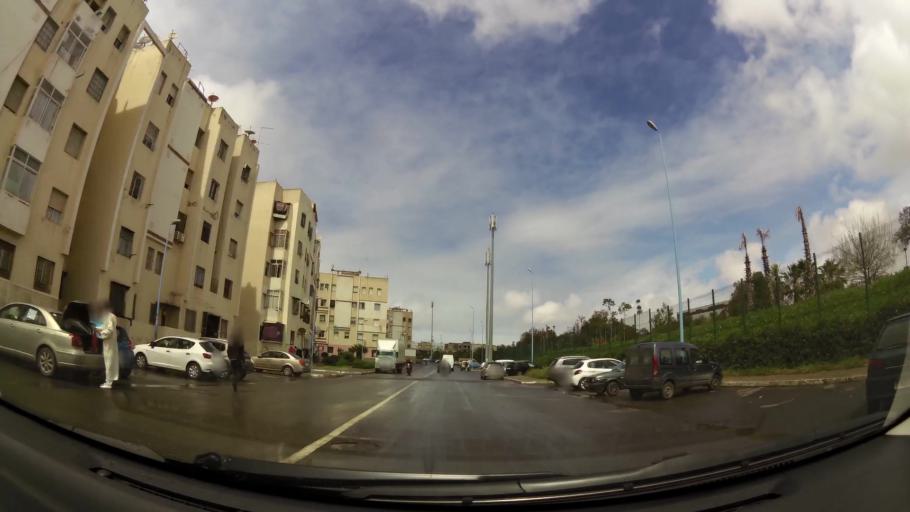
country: MA
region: Grand Casablanca
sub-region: Casablanca
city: Casablanca
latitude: 33.5252
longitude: -7.6453
